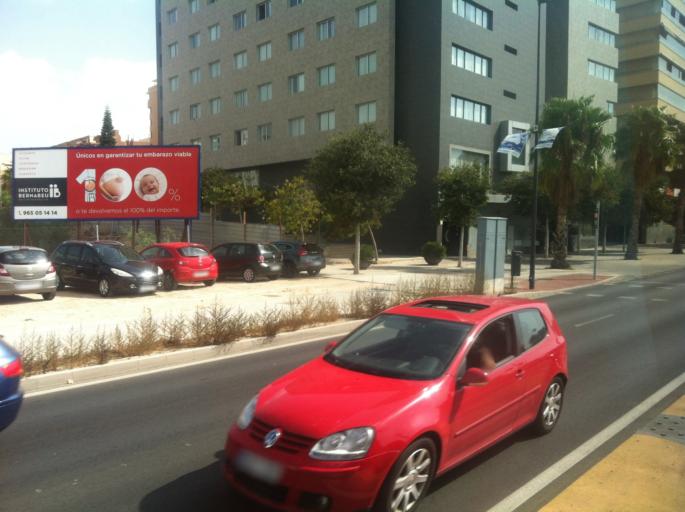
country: ES
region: Valencia
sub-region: Provincia de Alicante
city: Alicante
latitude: 38.3382
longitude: -0.4952
